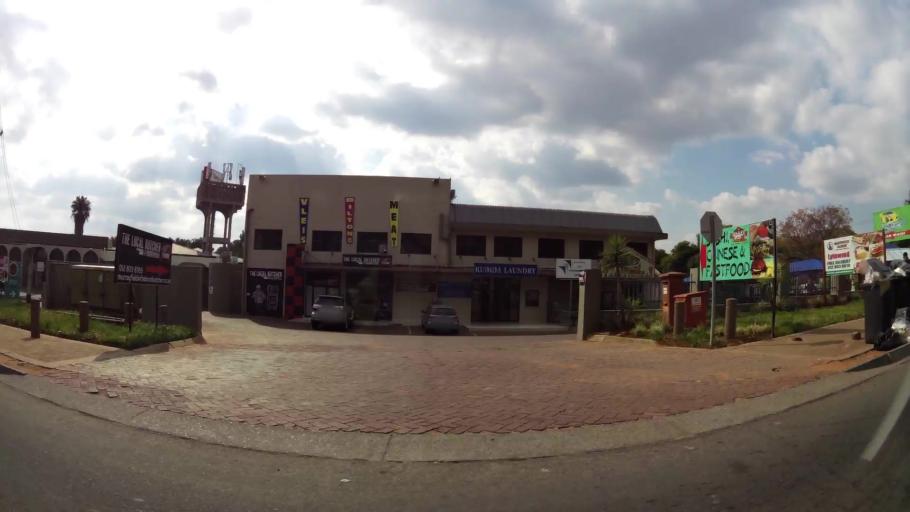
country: ZA
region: Gauteng
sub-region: City of Tshwane Metropolitan Municipality
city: Pretoria
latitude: -25.7556
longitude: 28.3057
